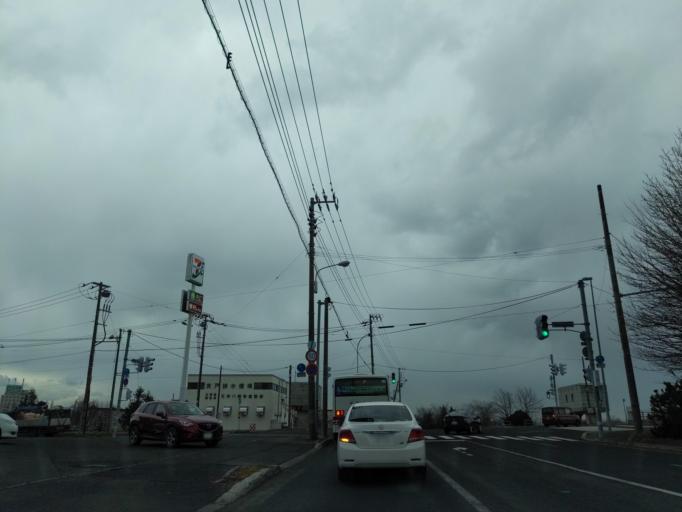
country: JP
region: Hokkaido
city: Ishikari
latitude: 43.1583
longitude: 141.3603
